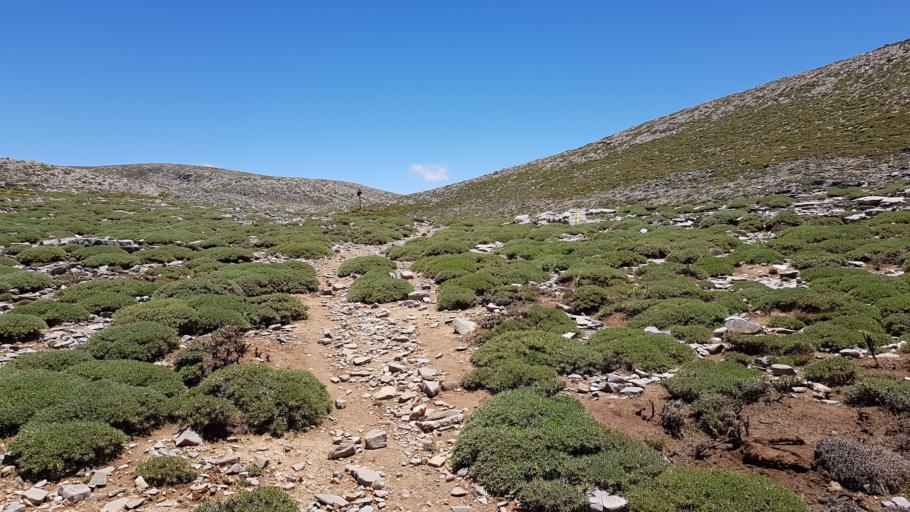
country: GR
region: Crete
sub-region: Nomos Rethymnis
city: Zoniana
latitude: 35.2215
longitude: 24.7926
